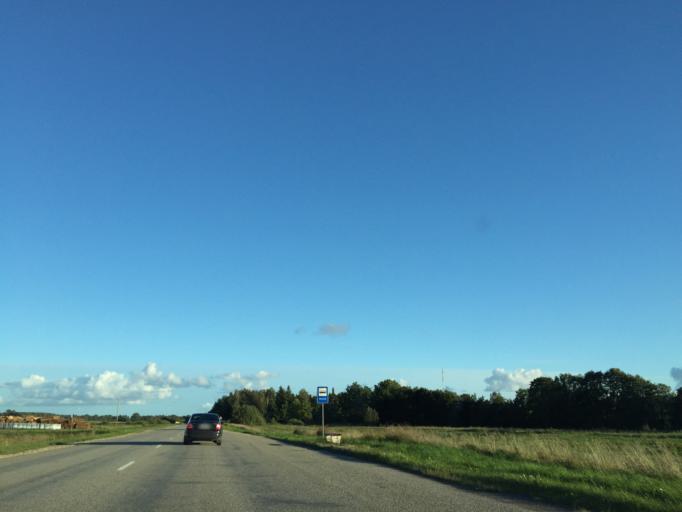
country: LV
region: Kuldigas Rajons
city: Kuldiga
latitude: 56.9560
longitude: 22.0068
